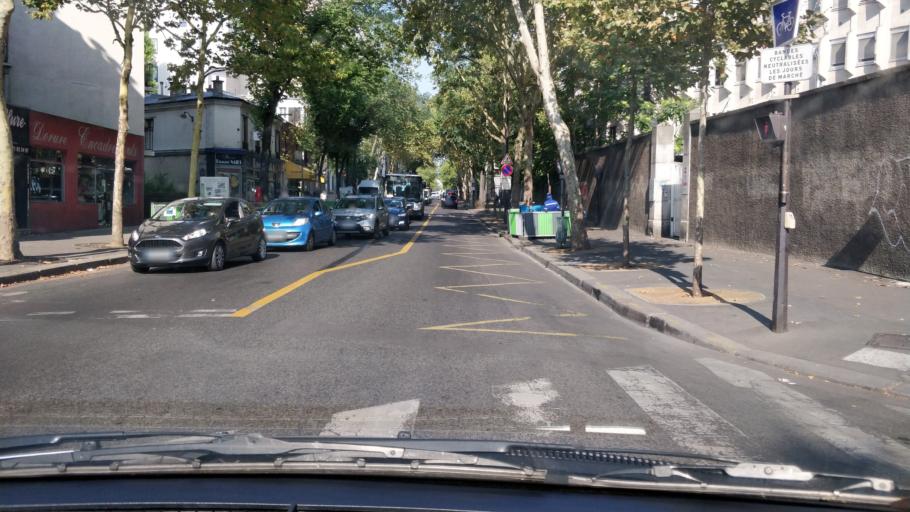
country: FR
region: Ile-de-France
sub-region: Departement de Seine-Saint-Denis
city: Bagnolet
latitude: 48.8647
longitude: 2.4041
